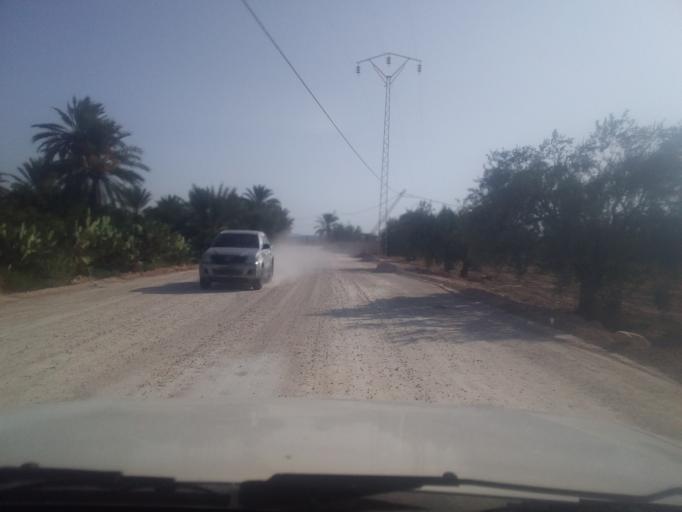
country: TN
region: Qabis
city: Matmata
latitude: 33.6010
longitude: 10.2760
